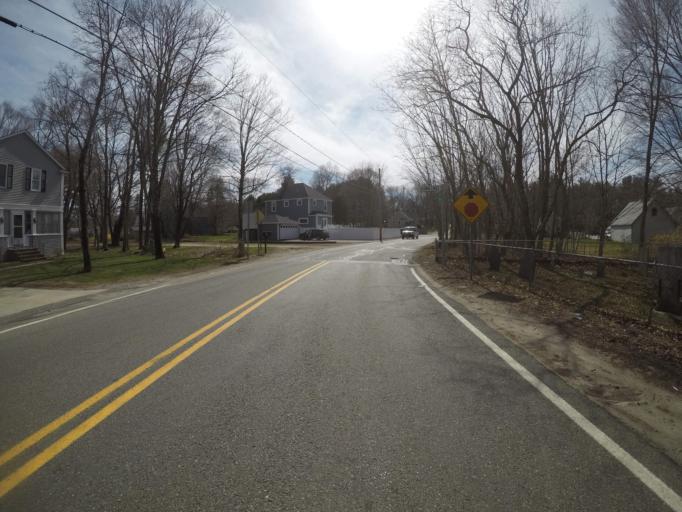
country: US
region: Massachusetts
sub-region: Plymouth County
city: West Bridgewater
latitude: 42.0375
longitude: -71.0667
